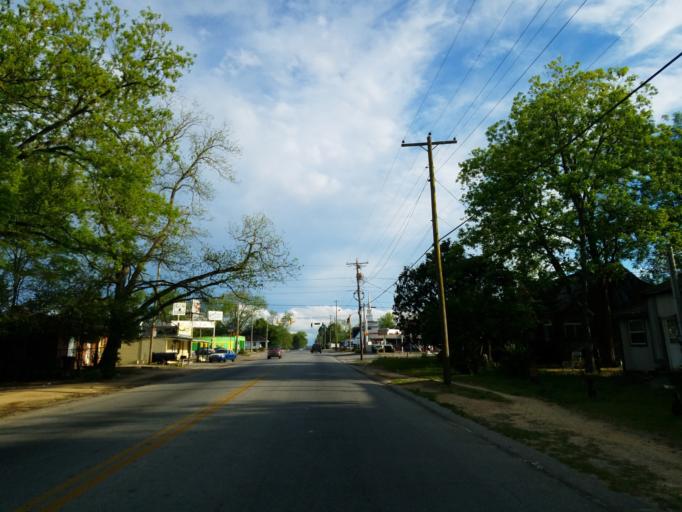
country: US
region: Georgia
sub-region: Crisp County
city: Cordele
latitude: 31.9645
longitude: -83.7880
